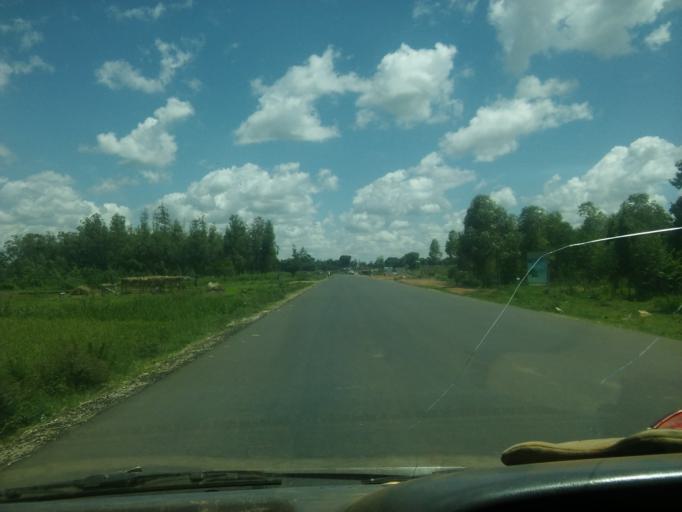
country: UG
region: Eastern Region
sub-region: Mbale District
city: Mbale
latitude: 1.0747
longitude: 34.1265
